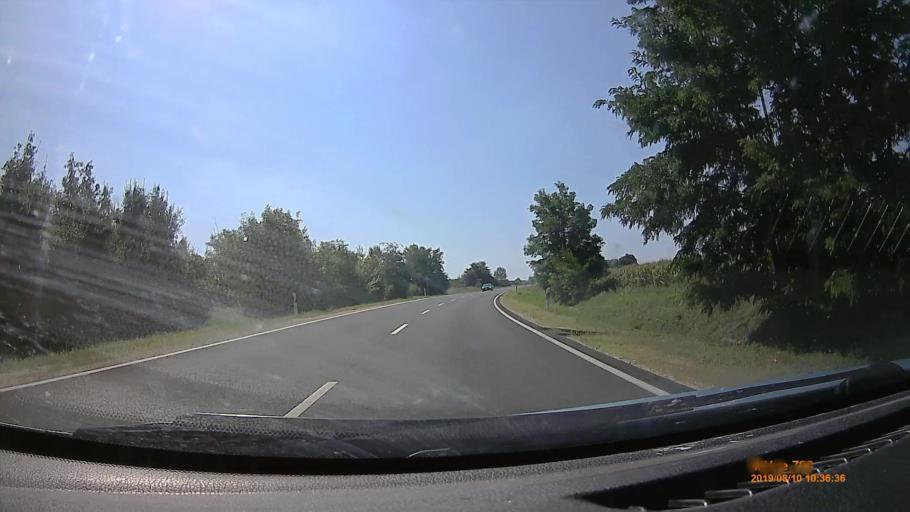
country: HU
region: Somogy
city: Balatonszarszo
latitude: 46.8265
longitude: 17.8526
